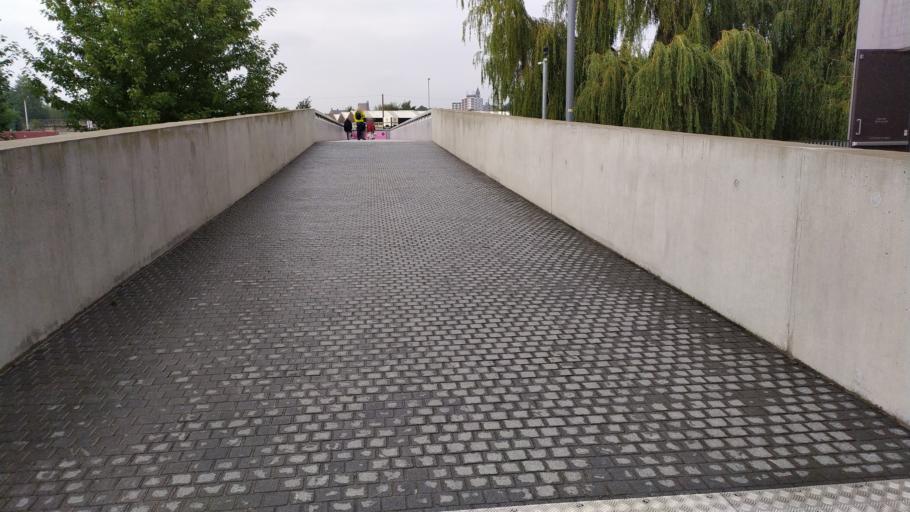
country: GB
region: England
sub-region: City and Borough of Wakefield
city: Wakefield
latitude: 53.6759
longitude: -1.4916
